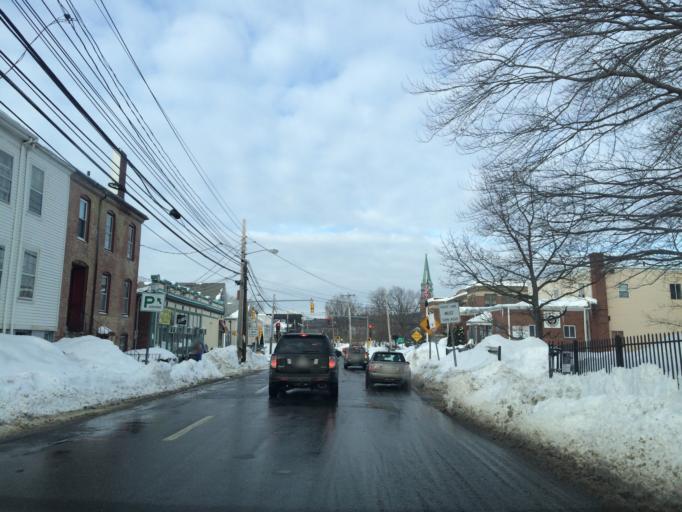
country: US
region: Massachusetts
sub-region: Middlesex County
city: Waltham
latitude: 42.3779
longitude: -71.2348
